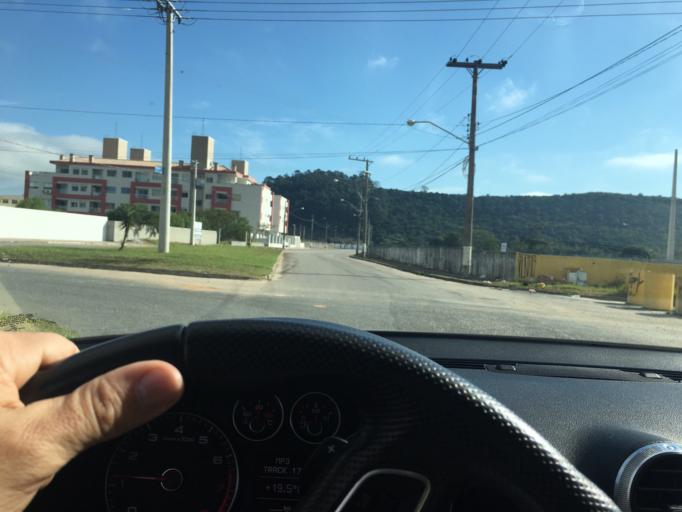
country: BR
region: Santa Catarina
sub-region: Florianopolis
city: Itacorubi
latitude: -27.4343
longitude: -48.4071
